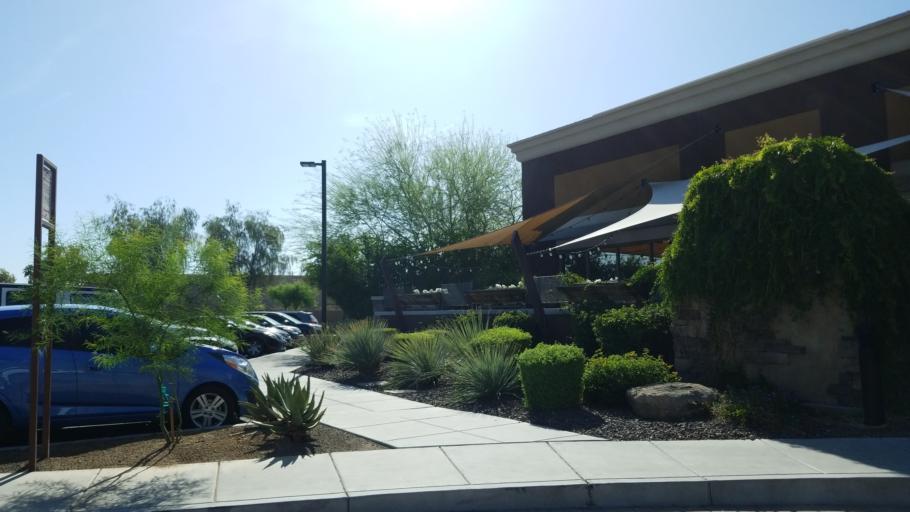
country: US
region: Arizona
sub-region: Maricopa County
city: Scottsdale
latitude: 33.5811
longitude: -111.8793
